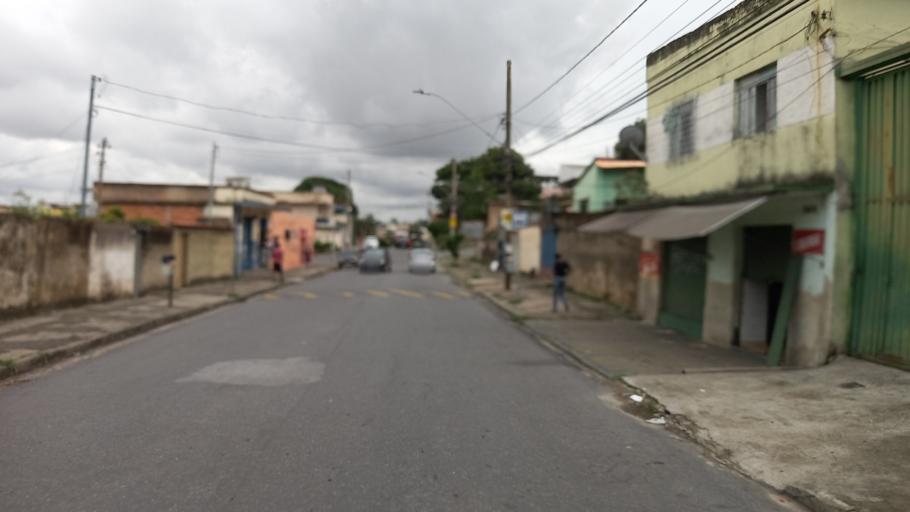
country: BR
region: Minas Gerais
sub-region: Belo Horizonte
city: Belo Horizonte
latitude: -19.8972
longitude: -43.8939
